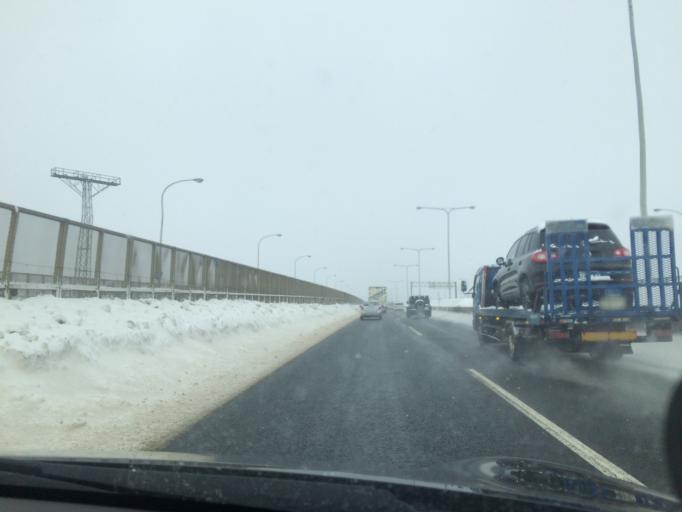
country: JP
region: Hokkaido
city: Sapporo
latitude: 43.0457
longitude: 141.4347
